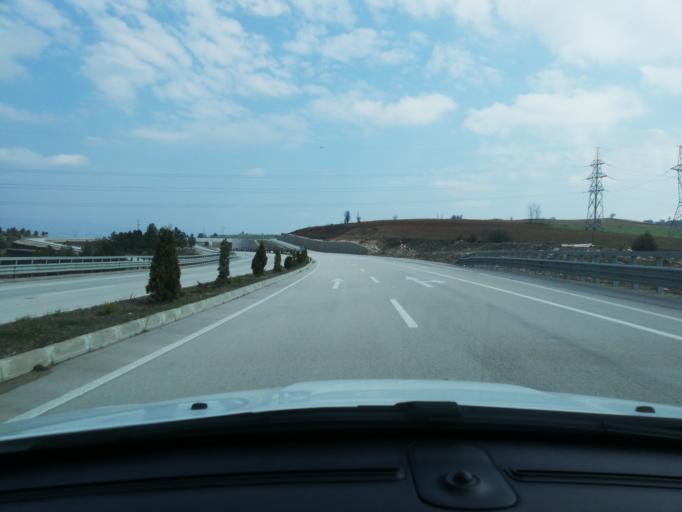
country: TR
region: Kastamonu
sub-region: Cide
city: Kastamonu
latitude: 41.3790
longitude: 33.8055
